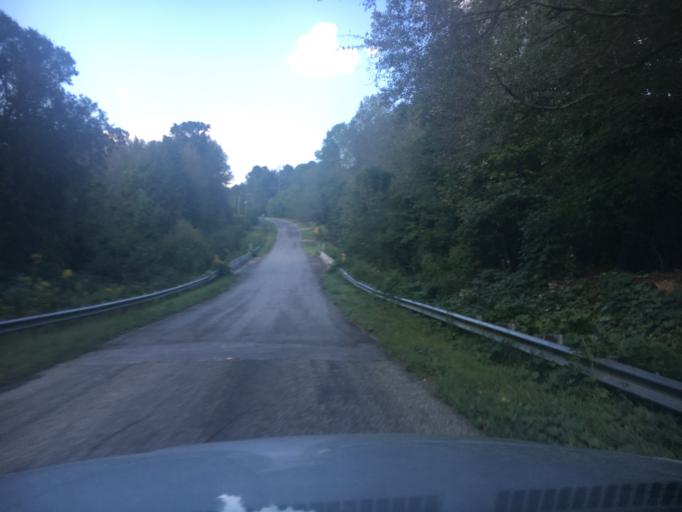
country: US
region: South Carolina
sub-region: Greenwood County
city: Ware Shoals
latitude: 34.4978
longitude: -82.2331
